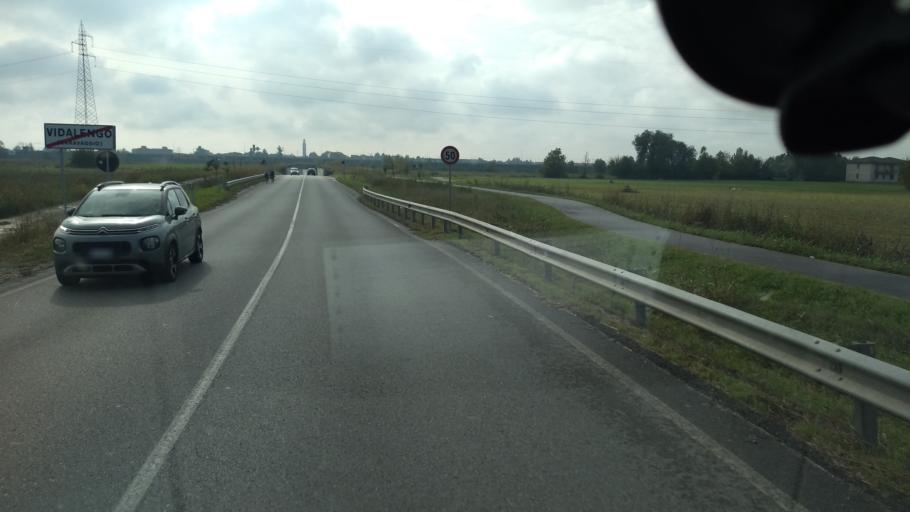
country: IT
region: Lombardy
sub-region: Provincia di Bergamo
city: Vidalengo
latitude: 45.5152
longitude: 9.6413
